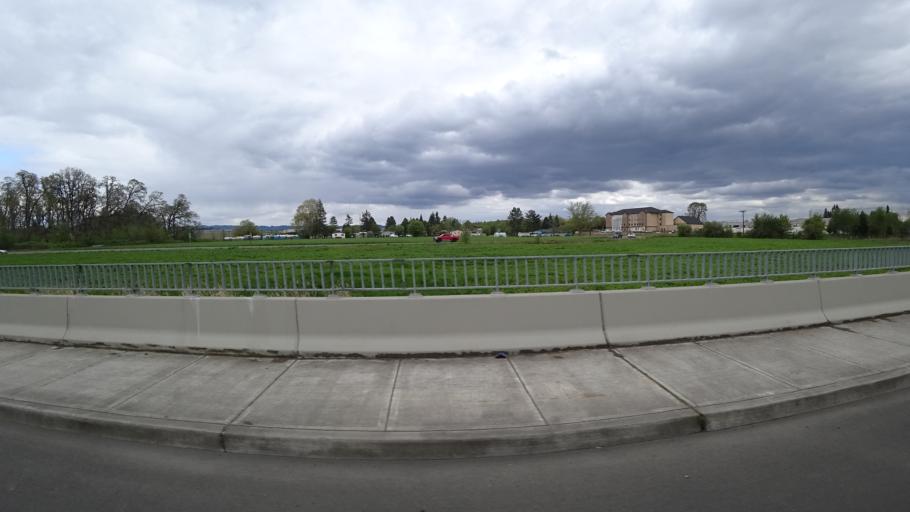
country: US
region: Oregon
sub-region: Washington County
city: Rockcreek
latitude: 45.5667
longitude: -122.9256
